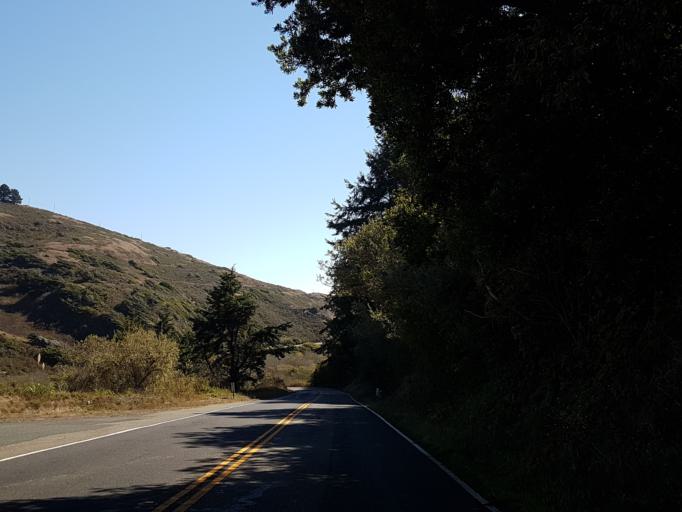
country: US
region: California
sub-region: Sonoma County
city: Monte Rio
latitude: 38.4730
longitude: -123.1555
